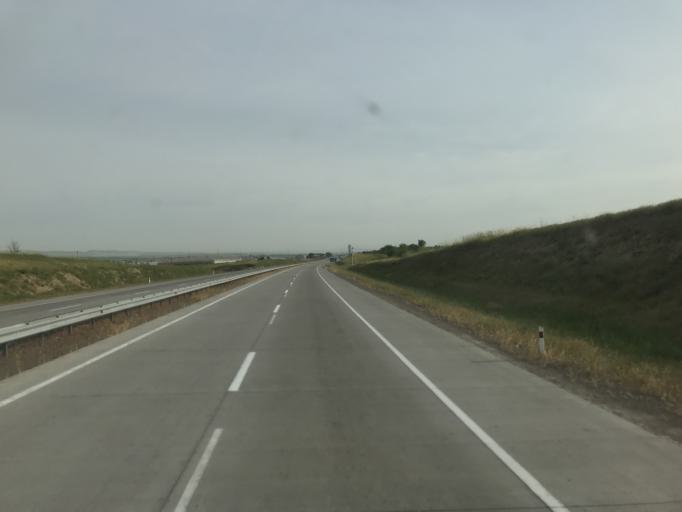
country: KZ
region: Ongtustik Qazaqstan
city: Qazyqurt
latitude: 41.6781
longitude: 69.3936
